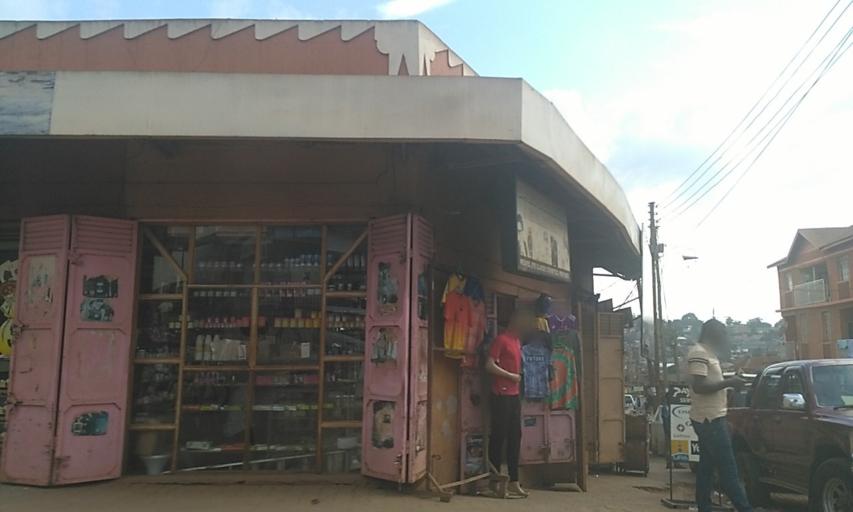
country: UG
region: Central Region
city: Kampala Central Division
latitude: 0.3129
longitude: 32.5677
